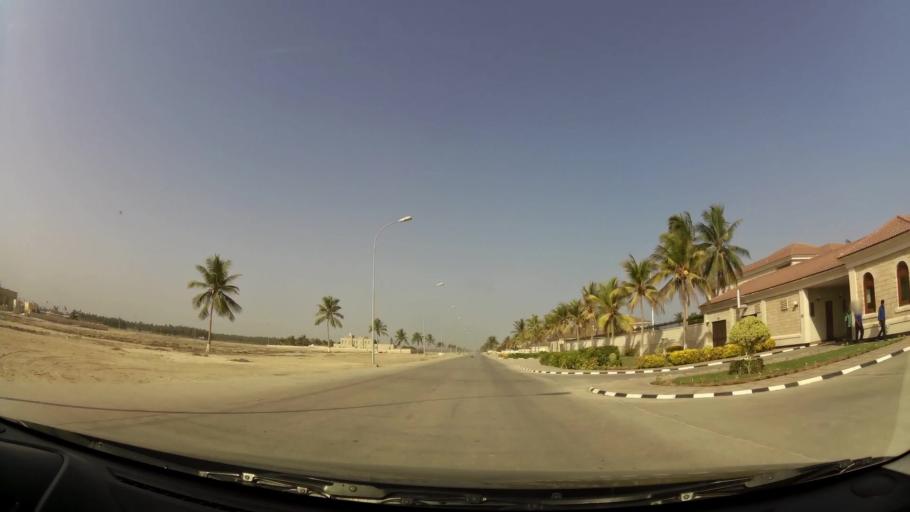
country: OM
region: Zufar
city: Salalah
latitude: 16.9930
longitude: 54.0483
